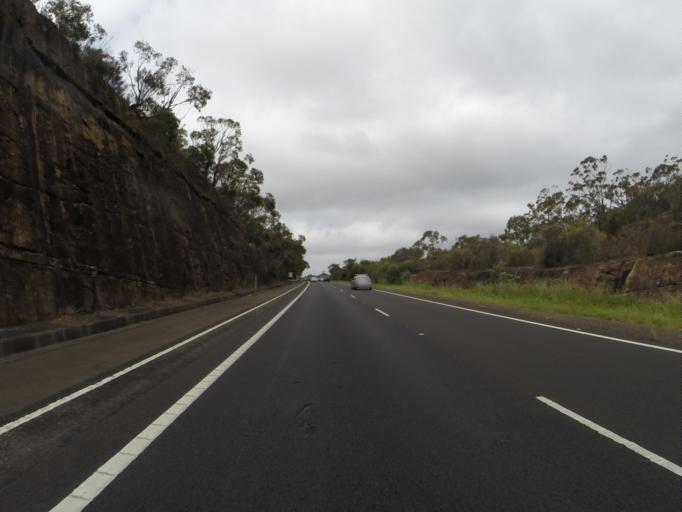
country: AU
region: New South Wales
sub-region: Wollongong
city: Helensburgh
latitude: -34.1553
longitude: 150.9865
